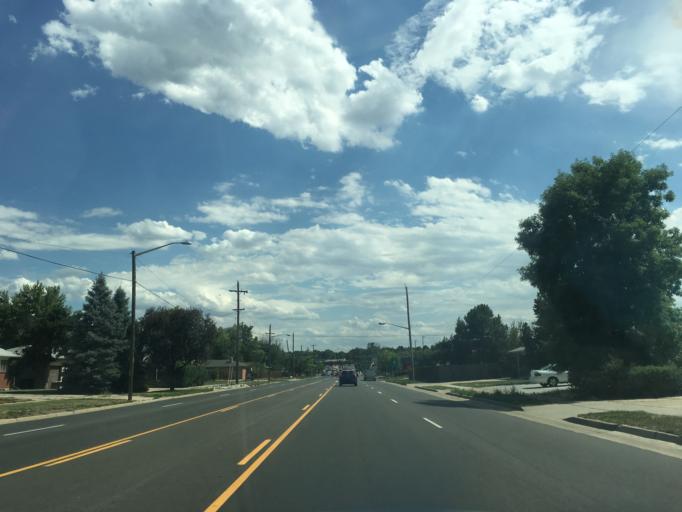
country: US
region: Colorado
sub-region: Arapahoe County
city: Sheridan
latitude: 39.6591
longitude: -105.0533
